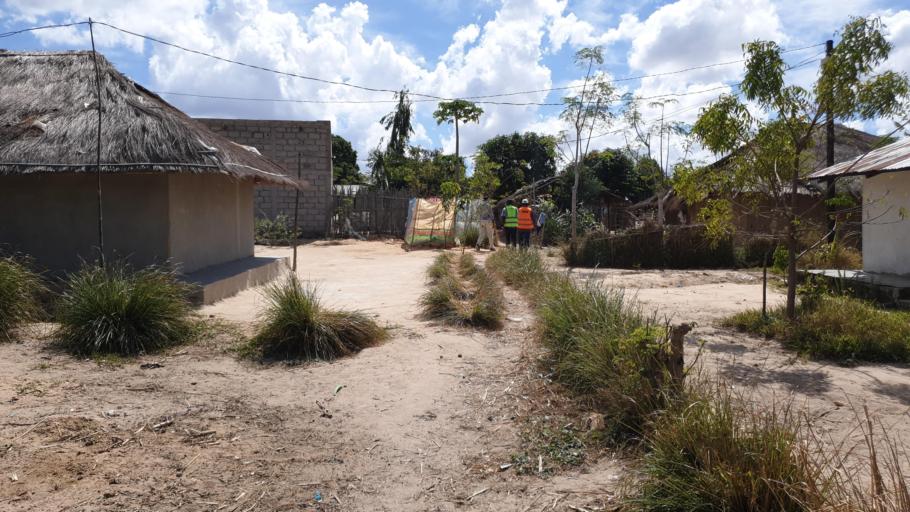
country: MZ
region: Nampula
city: Nacala
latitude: -14.5785
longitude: 40.7025
